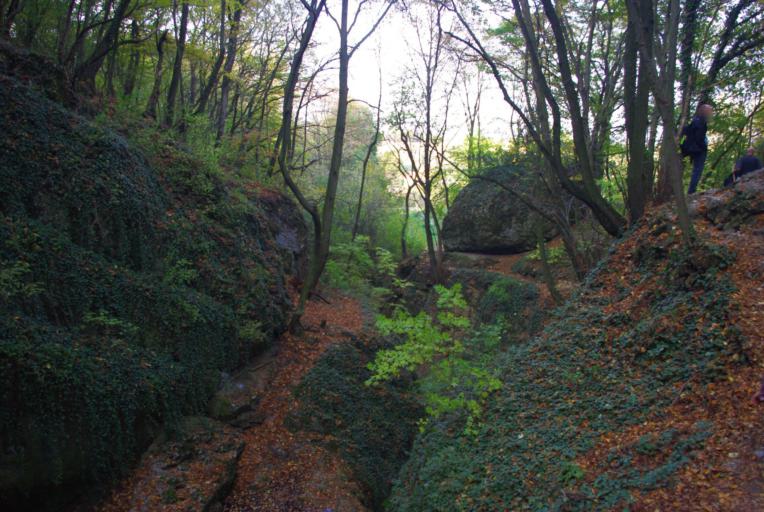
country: HU
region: Gyor-Moson-Sopron
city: Bakonyszentlaszlo
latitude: 47.3524
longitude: 17.8780
